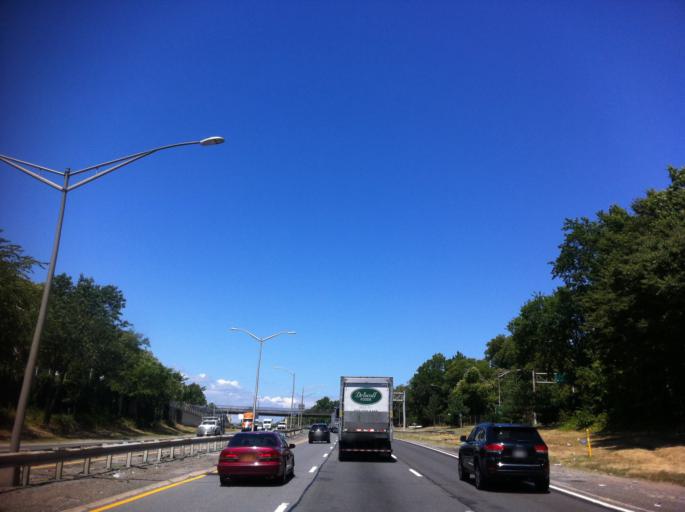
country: US
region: New York
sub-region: Nassau County
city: Bellerose Terrace
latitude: 40.7333
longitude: -73.7661
